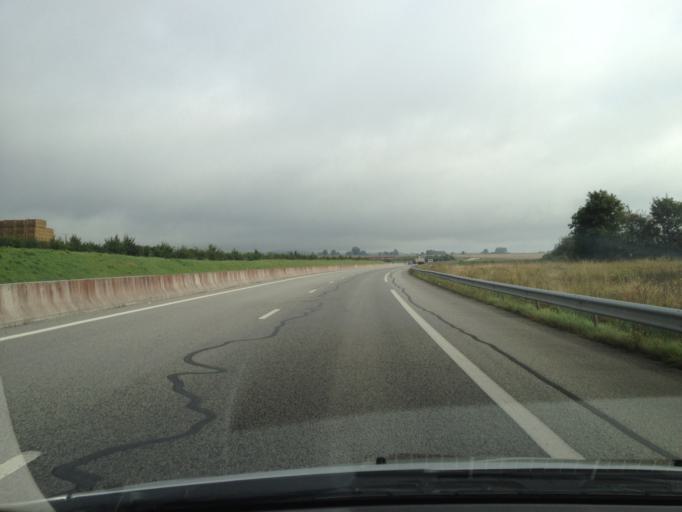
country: FR
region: Lower Normandy
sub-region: Departement de l'Orne
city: Valframbert
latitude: 48.4642
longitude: 0.1239
